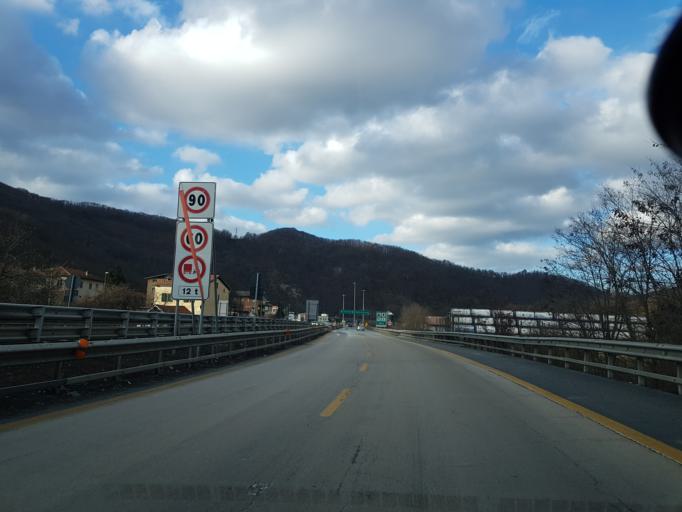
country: IT
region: Liguria
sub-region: Provincia di Genova
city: Ronco Scrivia
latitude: 44.5976
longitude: 8.9544
